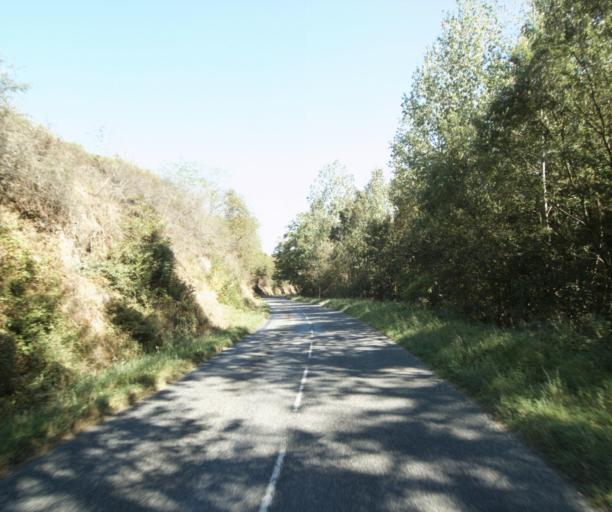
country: FR
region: Rhone-Alpes
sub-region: Departement du Rhone
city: Savigny
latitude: 45.8027
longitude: 4.5589
